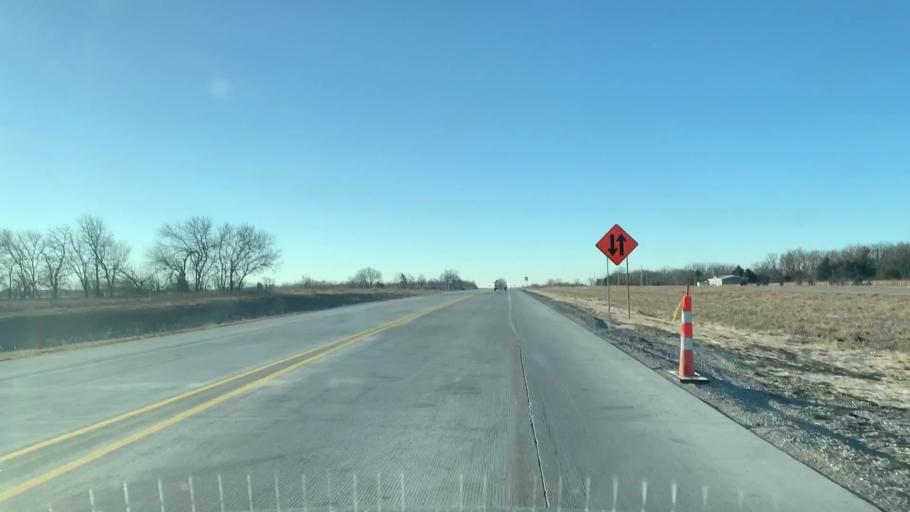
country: US
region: Kansas
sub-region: Bourbon County
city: Fort Scott
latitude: 37.7515
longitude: -94.7048
